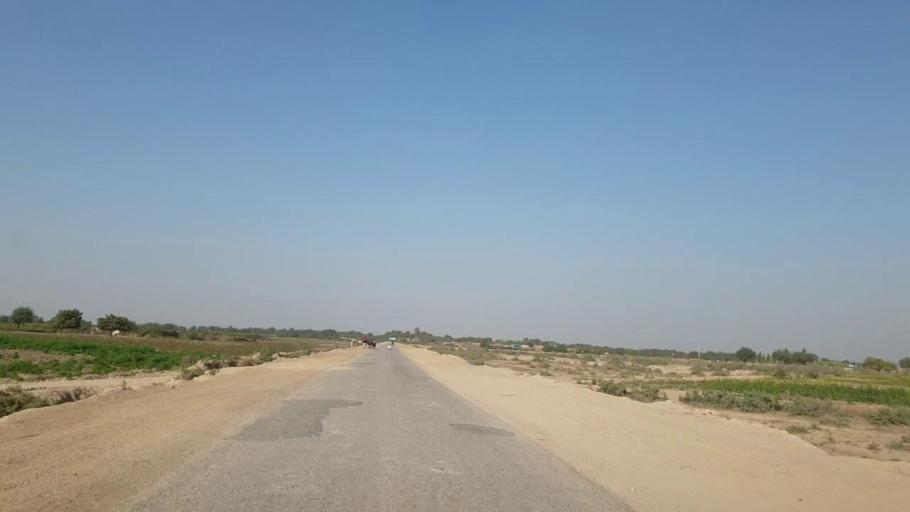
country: PK
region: Sindh
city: Digri
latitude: 25.1159
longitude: 69.1081
